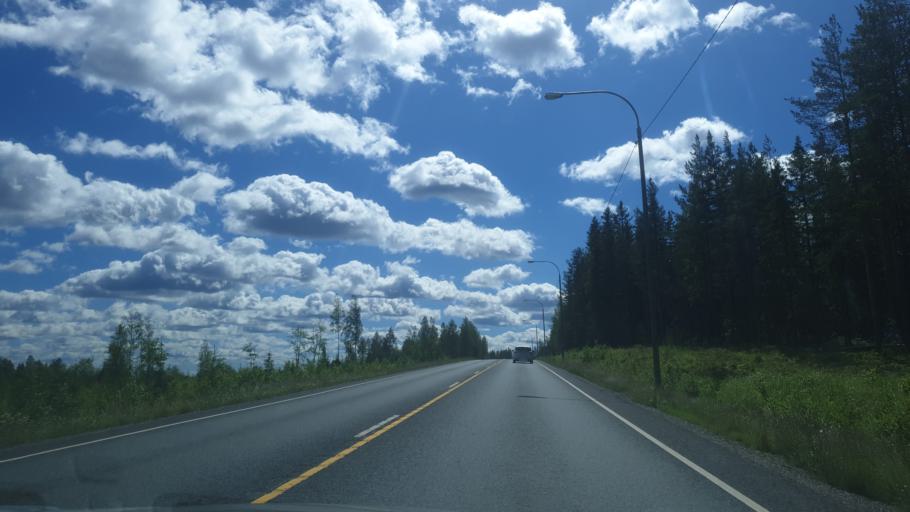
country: FI
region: Northern Savo
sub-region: Varkaus
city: Leppaevirta
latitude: 62.6307
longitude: 27.6169
